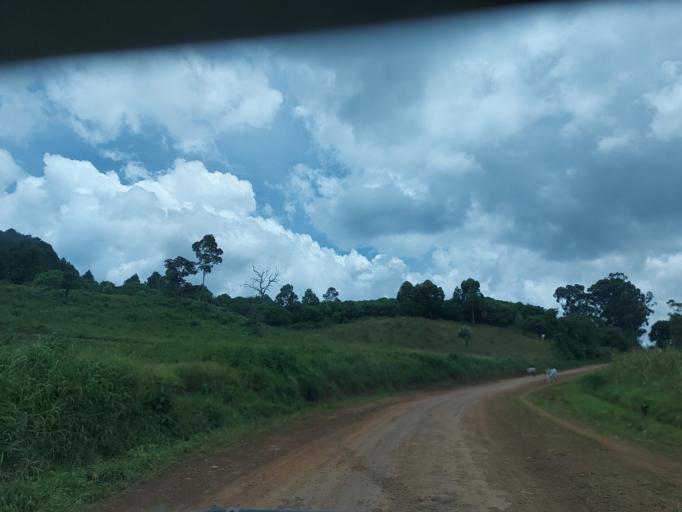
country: CD
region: South Kivu
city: Kabare
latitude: -2.3181
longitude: 28.7607
